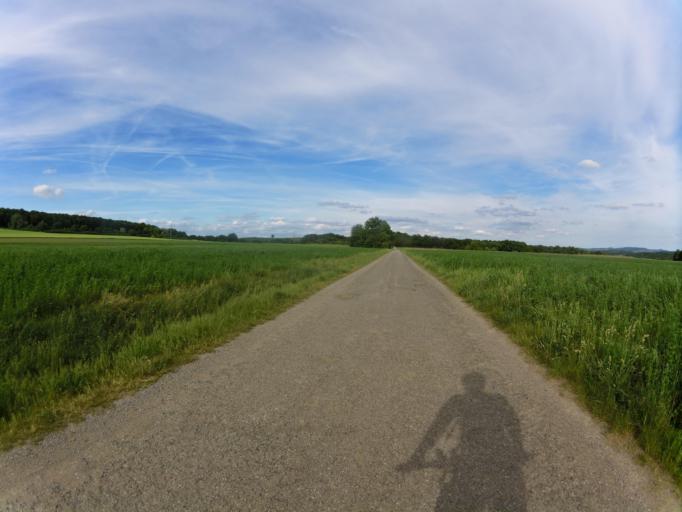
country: DE
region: Bavaria
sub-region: Regierungsbezirk Unterfranken
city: Ochsenfurt
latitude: 49.6749
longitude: 10.0682
